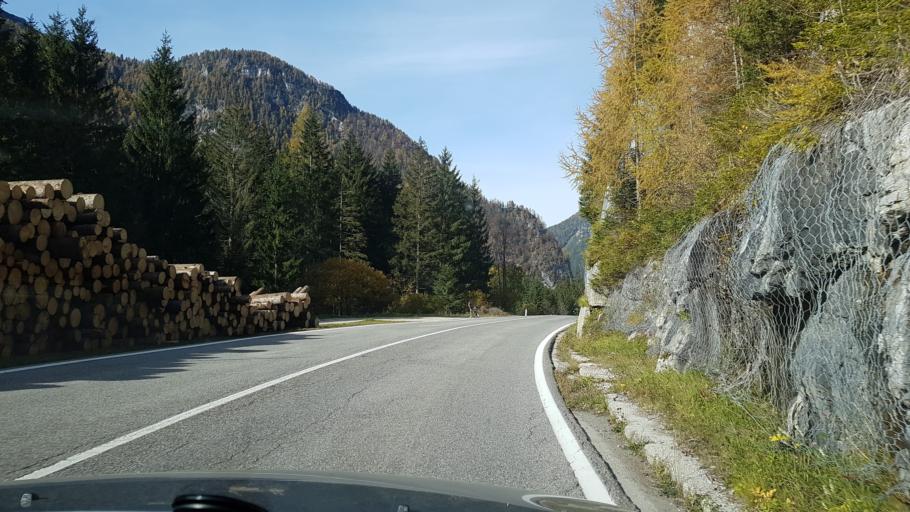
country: IT
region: Veneto
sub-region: Provincia di Belluno
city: Sappada
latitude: 46.5686
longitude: 12.6586
